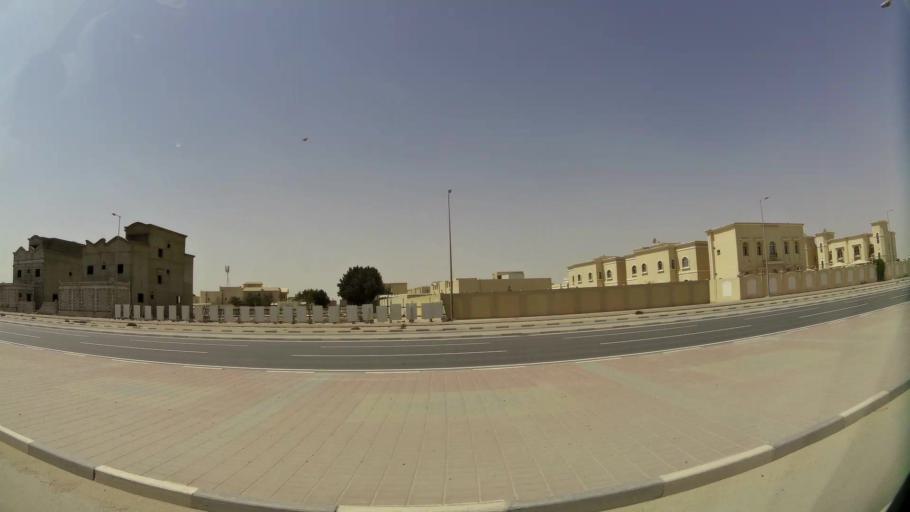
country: QA
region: Baladiyat Umm Salal
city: Umm Salal Muhammad
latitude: 25.3848
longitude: 51.4673
